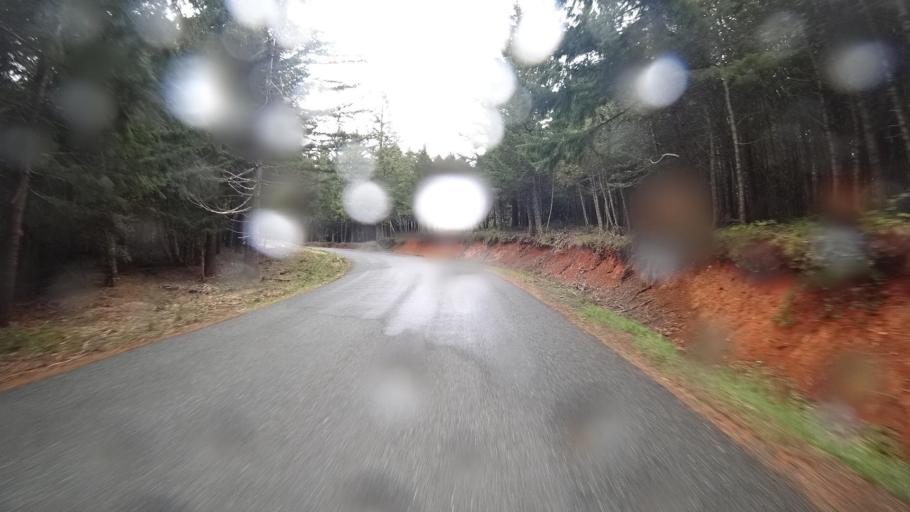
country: US
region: California
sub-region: Humboldt County
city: Willow Creek
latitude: 41.2004
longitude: -123.7940
